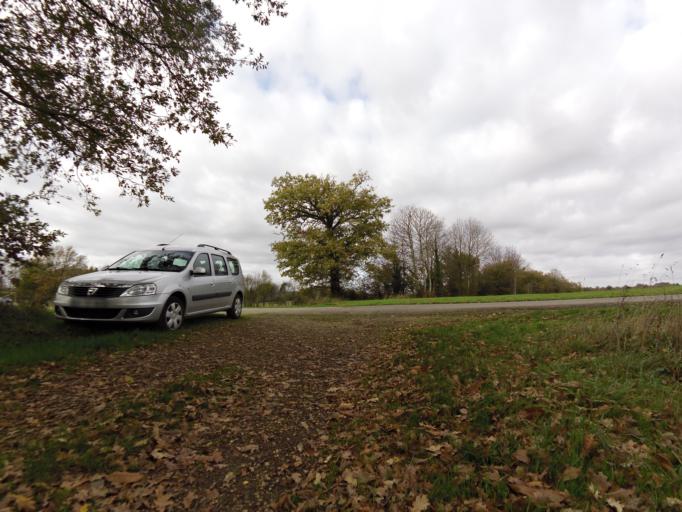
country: FR
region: Brittany
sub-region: Departement d'Ille-et-Vilaine
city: Orgeres
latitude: 47.9674
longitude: -1.6533
